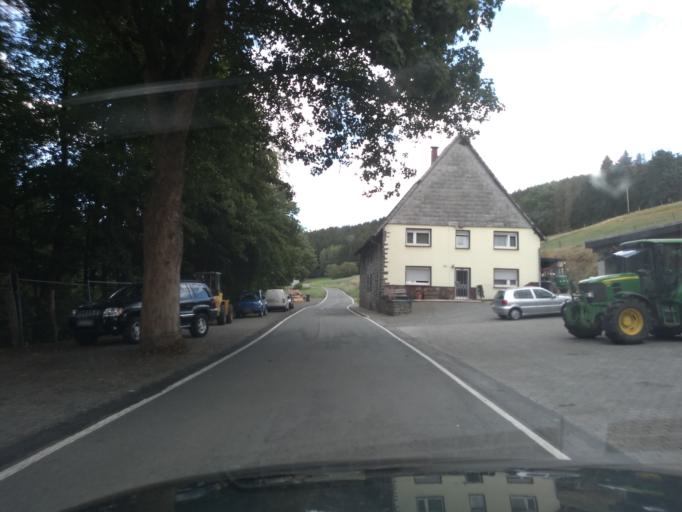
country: DE
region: North Rhine-Westphalia
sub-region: Regierungsbezirk Arnsberg
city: Schalksmuhle
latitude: 51.2323
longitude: 7.5737
